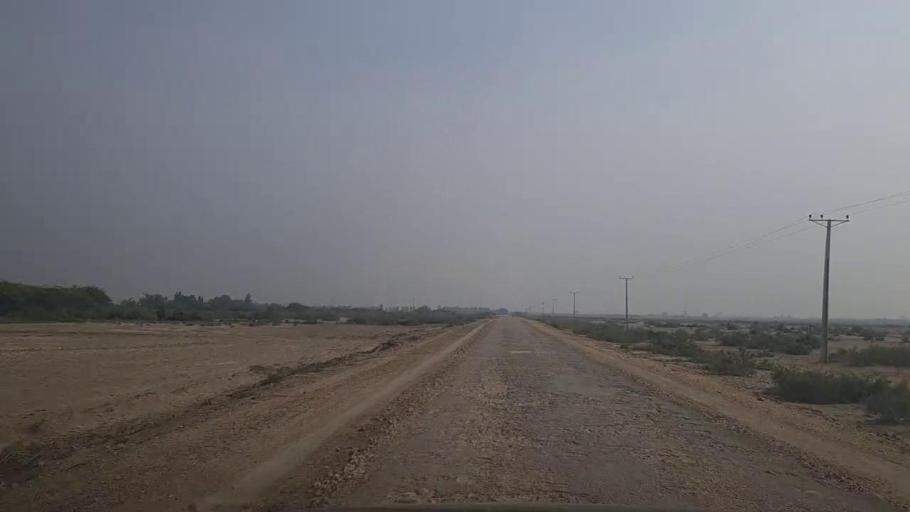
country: PK
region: Sindh
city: Mirpur Sakro
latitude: 24.4590
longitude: 67.6977
